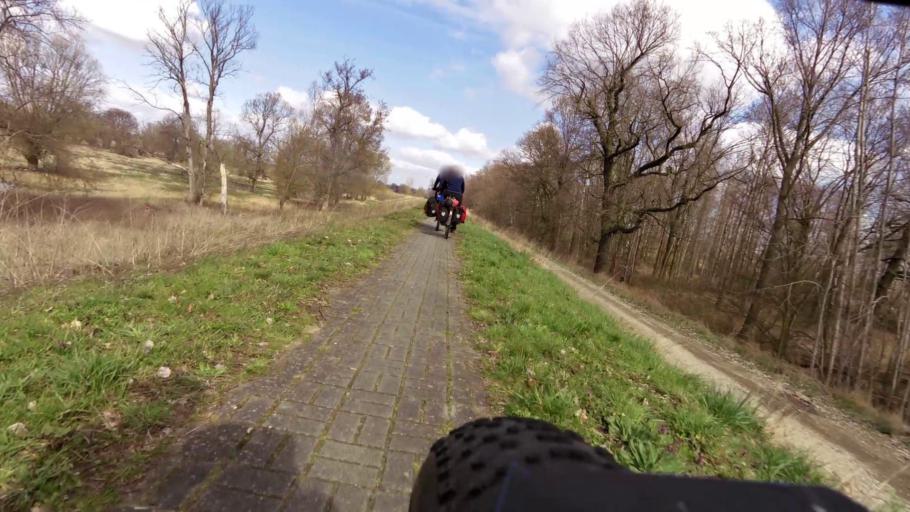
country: DE
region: Brandenburg
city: Lebus
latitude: 52.4027
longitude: 14.5450
